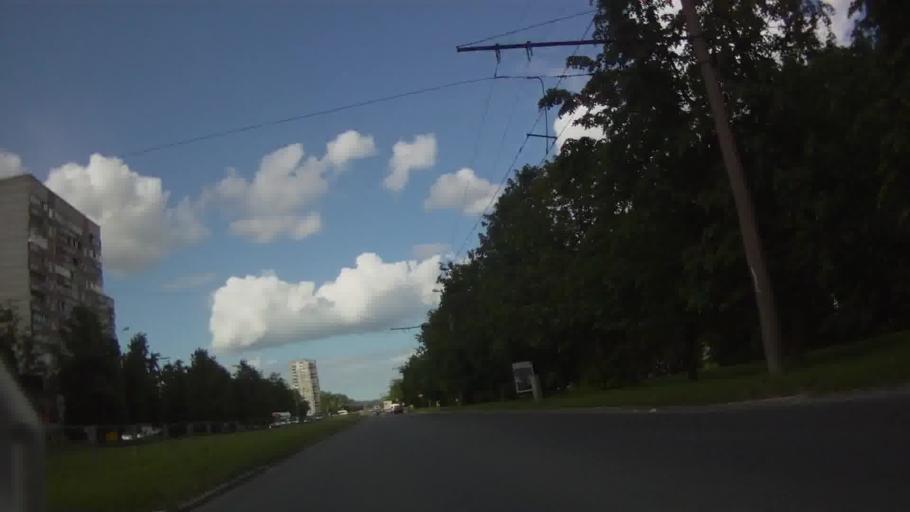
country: LV
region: Stopini
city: Ulbroka
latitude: 56.9355
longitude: 24.2025
